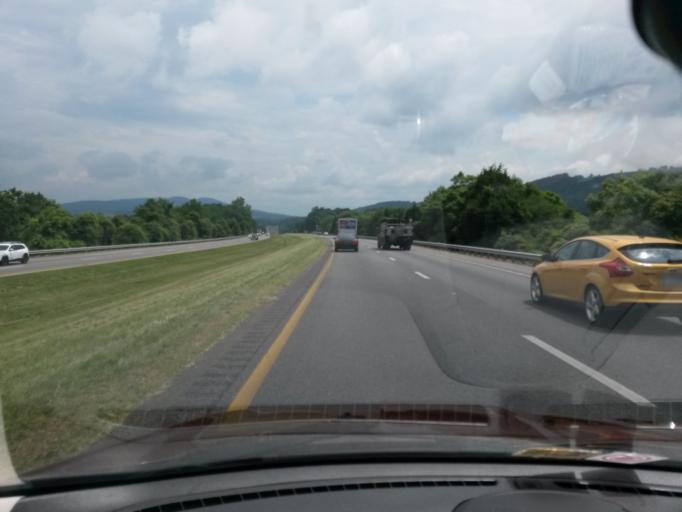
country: US
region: Virginia
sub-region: City of Charlottesville
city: Charlottesville
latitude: 38.0073
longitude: -78.4900
